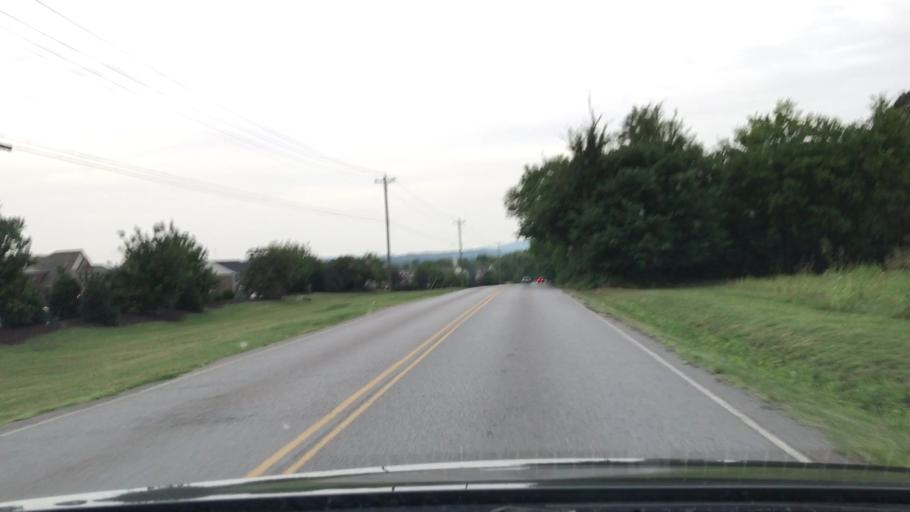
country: US
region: Tennessee
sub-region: Williamson County
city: Nolensville
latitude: 35.9490
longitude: -86.6433
